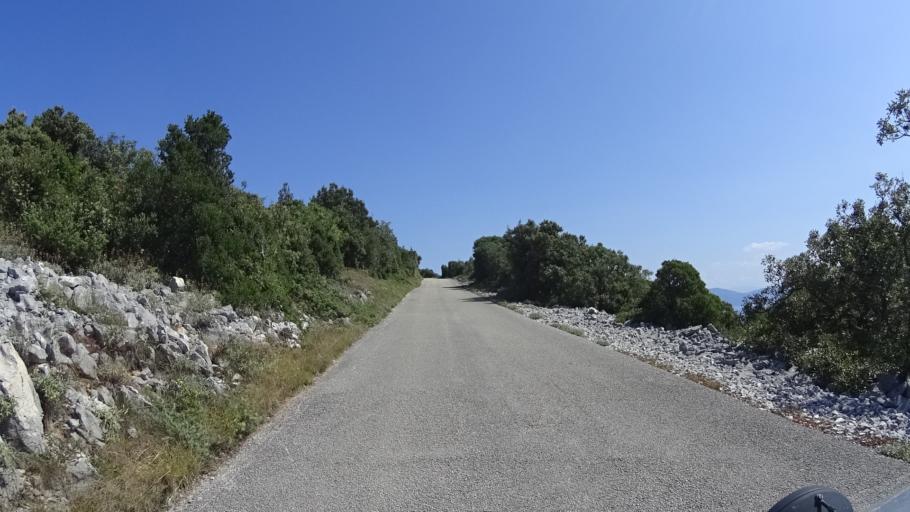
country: HR
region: Istarska
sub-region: Grad Labin
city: Rabac
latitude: 44.9696
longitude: 14.1461
